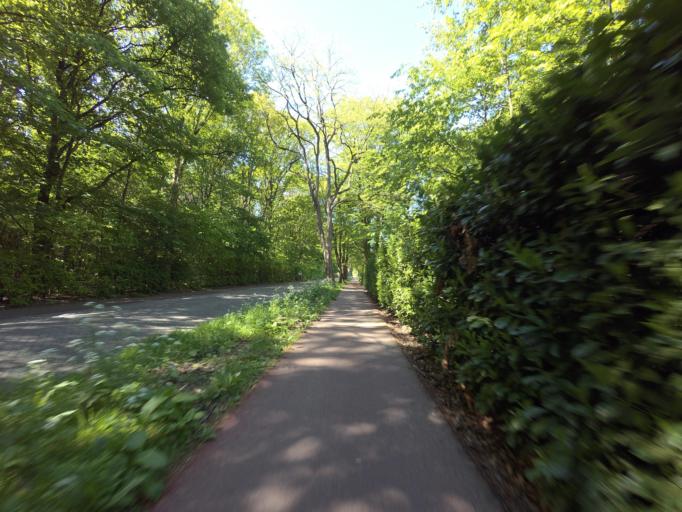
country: NL
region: North Brabant
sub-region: Gemeente Rucphen
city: Rucphen
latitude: 51.5634
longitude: 4.5498
